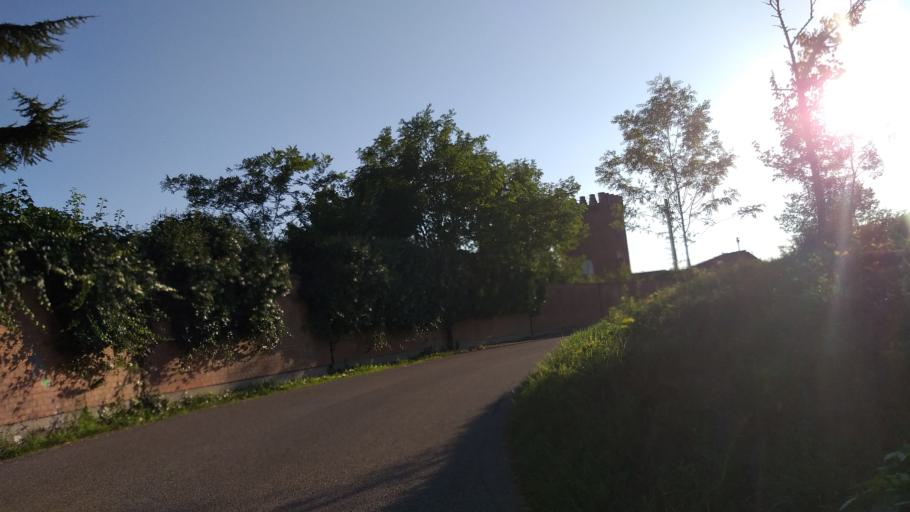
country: IT
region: Piedmont
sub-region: Provincia di Asti
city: Asti
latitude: 44.9239
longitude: 8.1911
